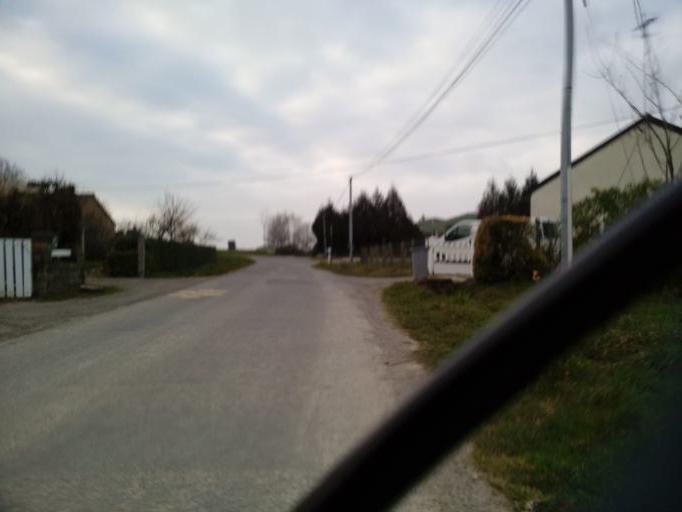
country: FR
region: Brittany
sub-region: Departement d'Ille-et-Vilaine
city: Talensac
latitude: 48.1142
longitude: -1.9029
